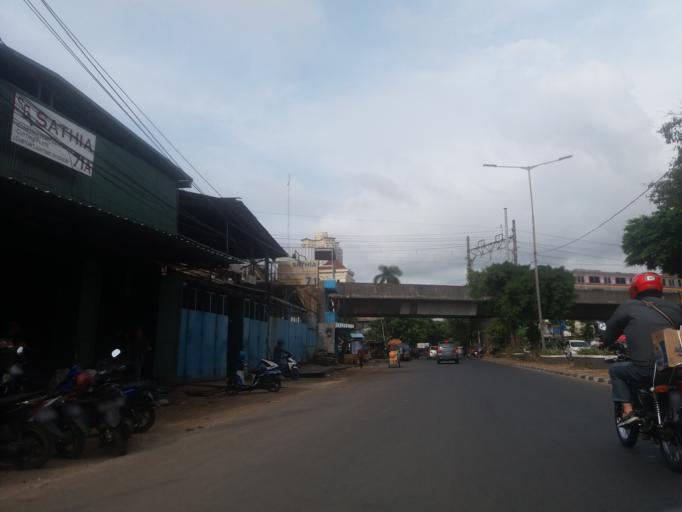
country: ID
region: Jakarta Raya
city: Jakarta
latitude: -6.1402
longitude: 106.8220
